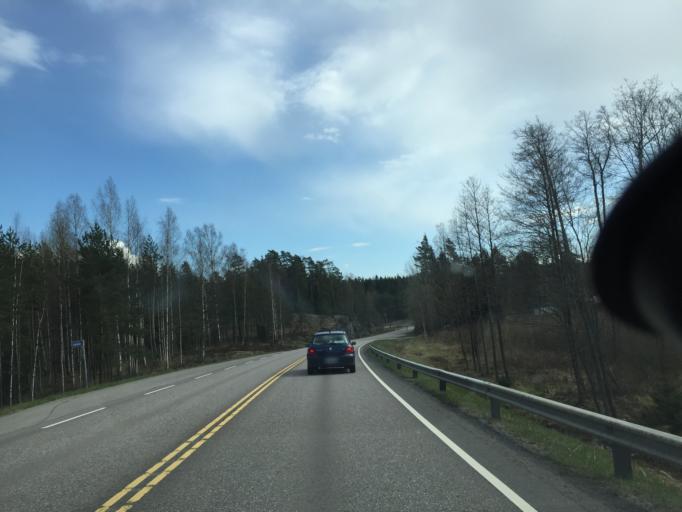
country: FI
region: Uusimaa
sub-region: Raaseporin
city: Ekenaes
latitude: 60.0350
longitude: 23.3661
